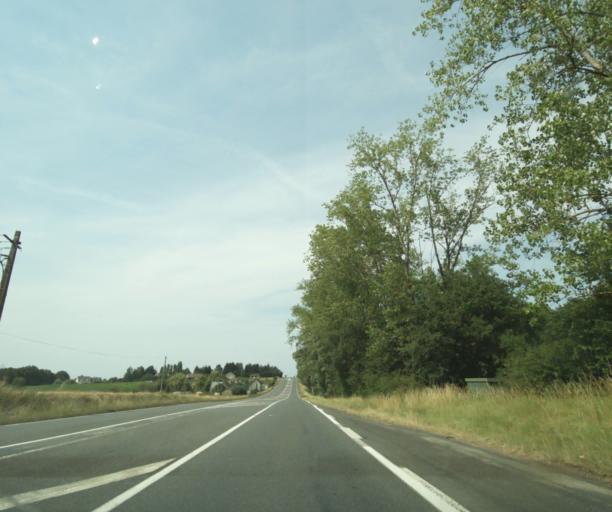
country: FR
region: Centre
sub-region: Departement d'Indre-et-Loire
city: Sainte-Maure-de-Touraine
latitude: 47.1480
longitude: 0.6468
